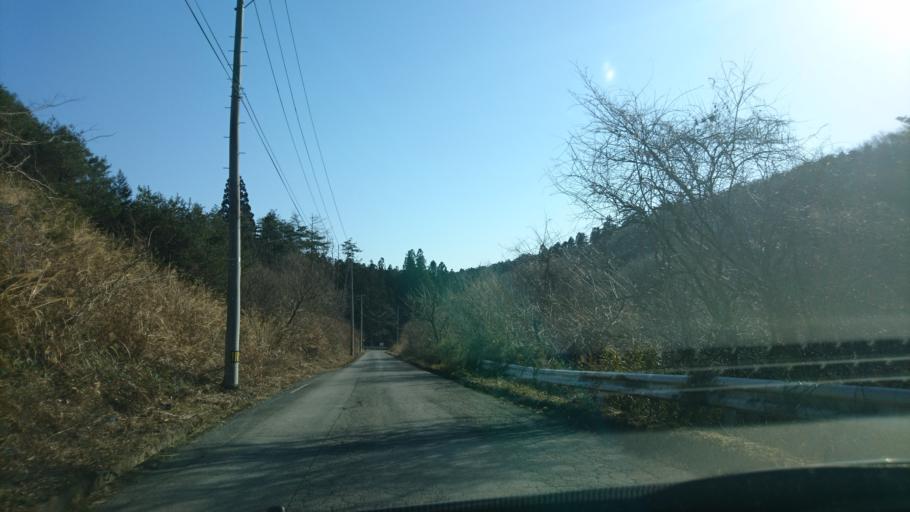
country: JP
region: Iwate
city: Ichinoseki
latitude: 38.8044
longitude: 141.2651
